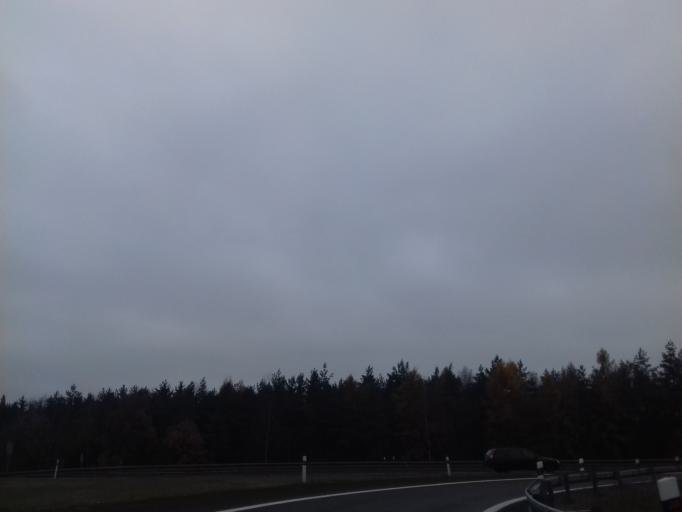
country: CZ
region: Plzensky
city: Vejprnice
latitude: 49.7097
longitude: 13.2818
